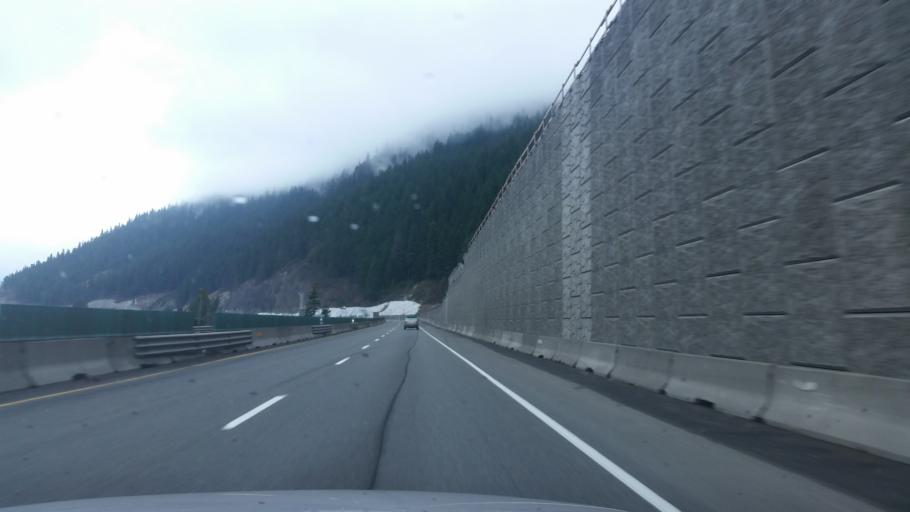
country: US
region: Washington
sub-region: King County
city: Tanner
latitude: 47.3463
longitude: -121.3641
